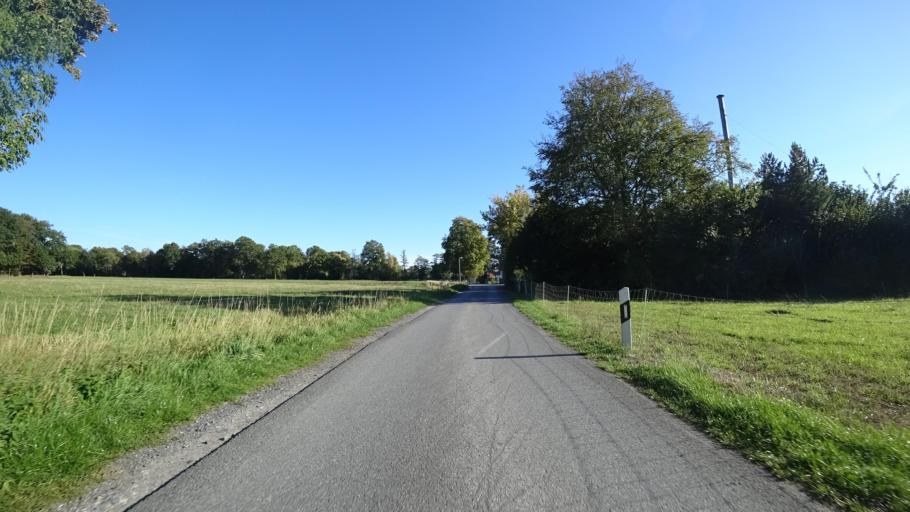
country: DE
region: North Rhine-Westphalia
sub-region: Regierungsbezirk Detmold
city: Guetersloh
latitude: 51.8750
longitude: 8.3618
